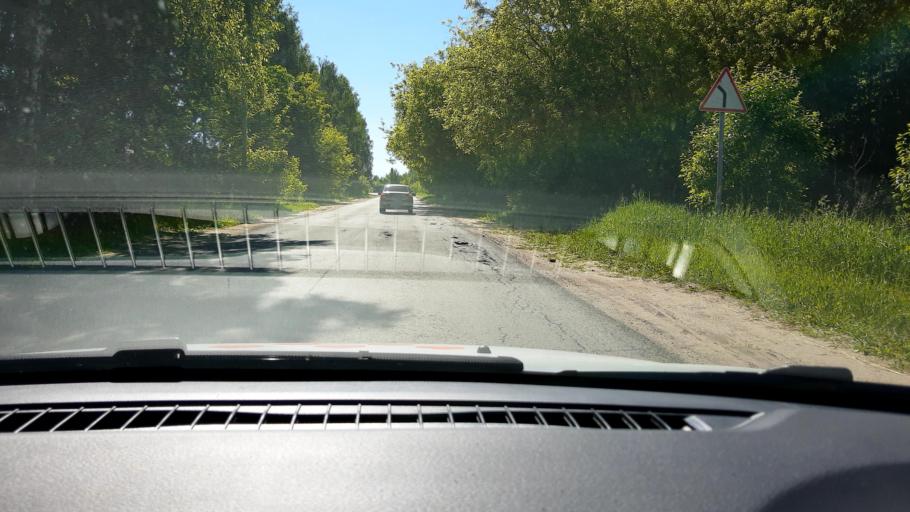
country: RU
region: Nizjnij Novgorod
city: Bor
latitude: 56.3845
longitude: 44.1473
